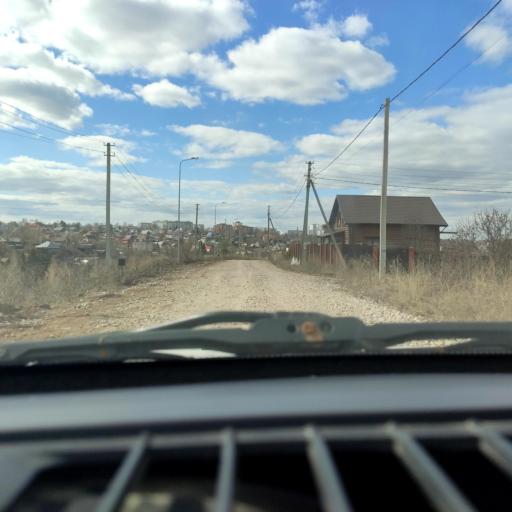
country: RU
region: Perm
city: Perm
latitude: 58.0247
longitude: 56.3489
